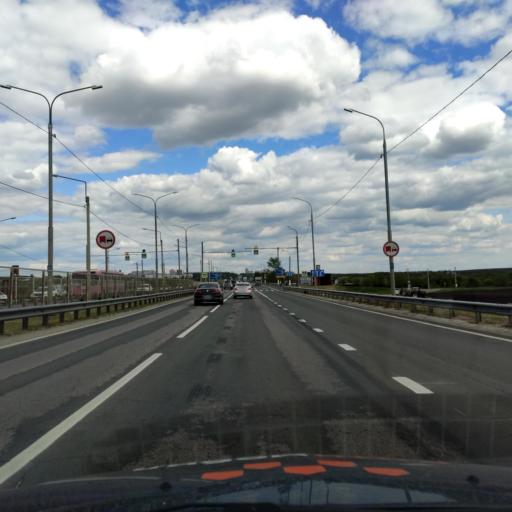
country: RU
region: Voronezj
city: Pridonskoy
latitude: 51.6508
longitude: 39.0609
